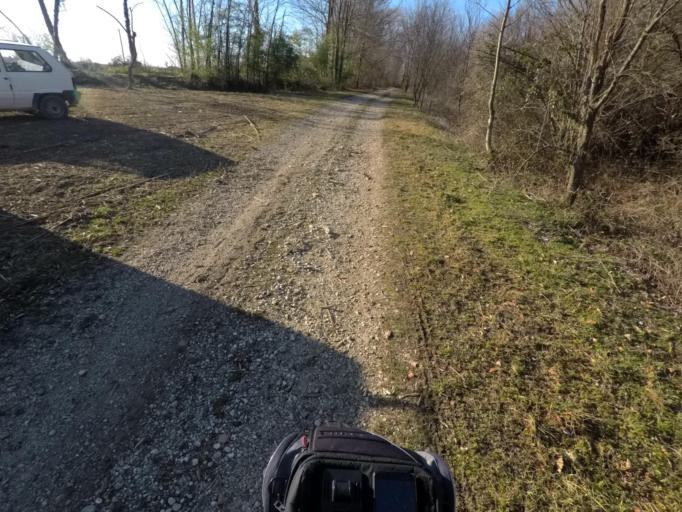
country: IT
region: Friuli Venezia Giulia
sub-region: Provincia di Udine
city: Remanzacco
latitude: 46.0988
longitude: 13.3270
